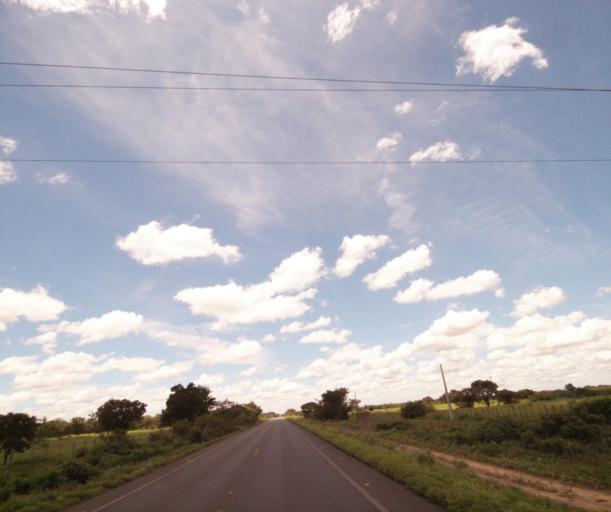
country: BR
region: Bahia
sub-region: Bom Jesus Da Lapa
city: Bom Jesus da Lapa
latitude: -13.2609
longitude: -43.5140
